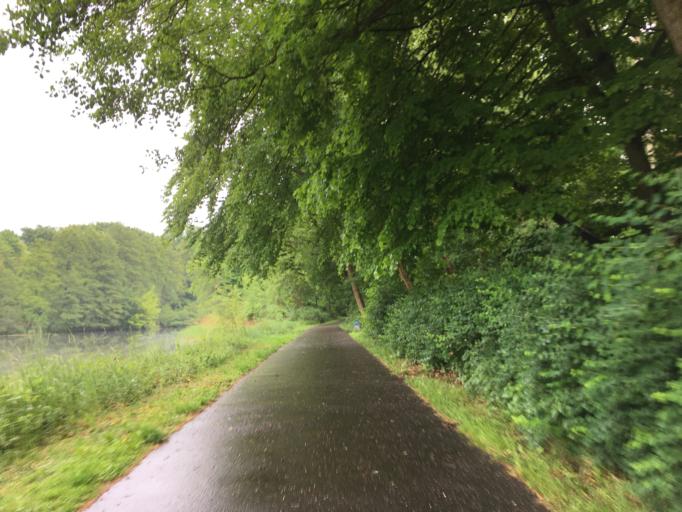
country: DE
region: Brandenburg
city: Eberswalde
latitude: 52.8423
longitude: 13.7842
